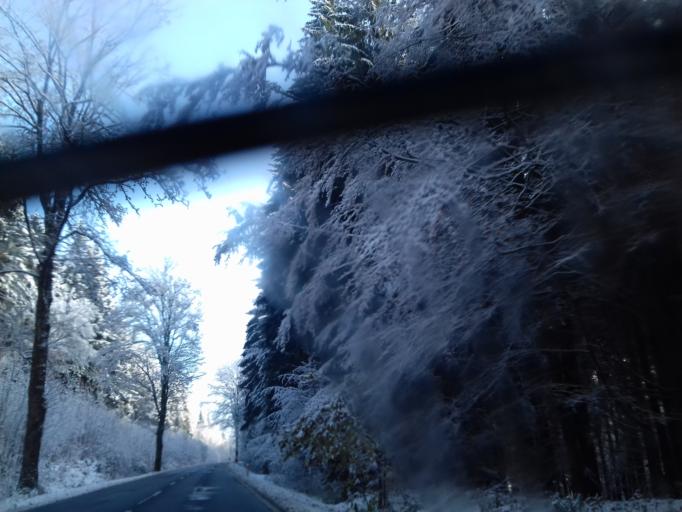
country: CZ
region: Plzensky
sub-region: Okres Domazlice
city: Klenci pod Cerchovem
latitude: 49.4124
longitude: 12.7975
